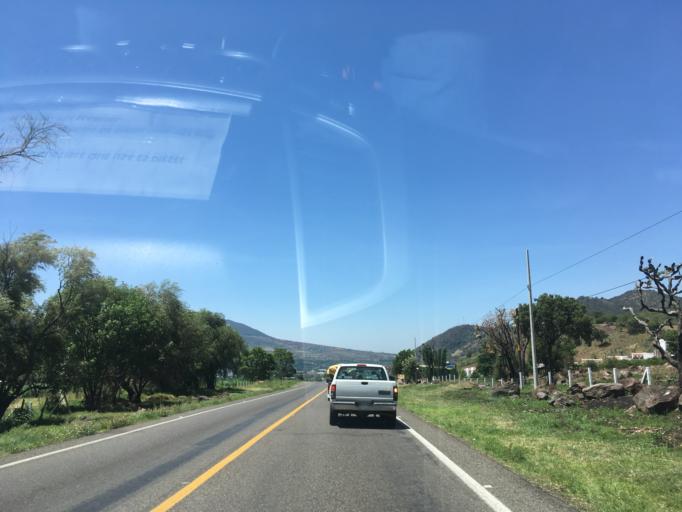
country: MX
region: Michoacan
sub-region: Tuxpan
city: Santa Ana
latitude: 19.6000
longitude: -100.4657
